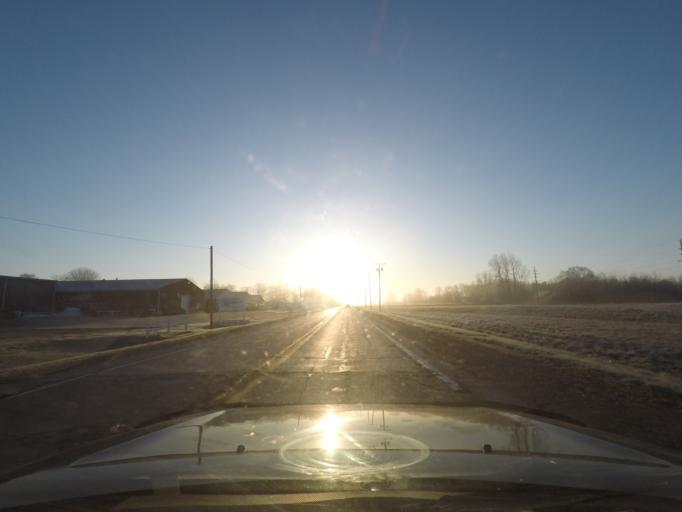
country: US
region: Indiana
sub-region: Marshall County
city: Bremen
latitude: 41.4542
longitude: -86.1276
